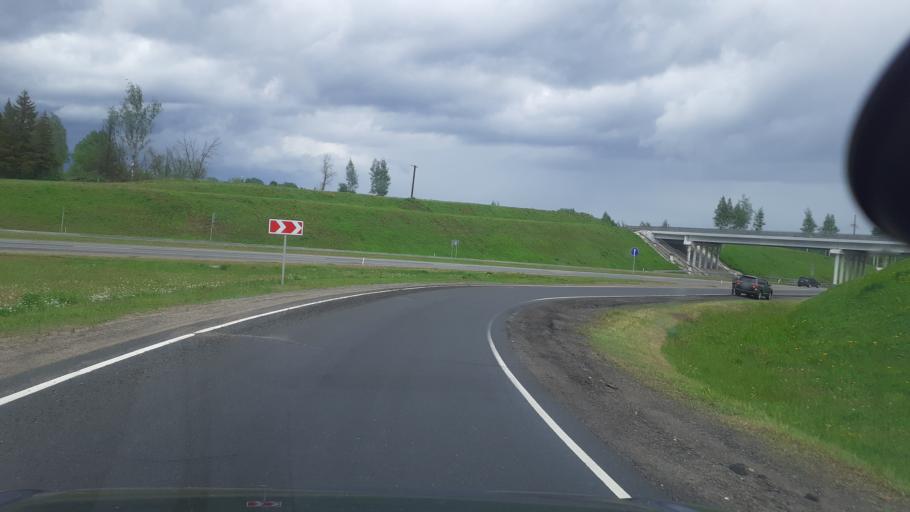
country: RU
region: Moskovskaya
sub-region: Volokolamskiy Rayon
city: Volokolamsk
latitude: 56.0204
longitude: 35.9644
